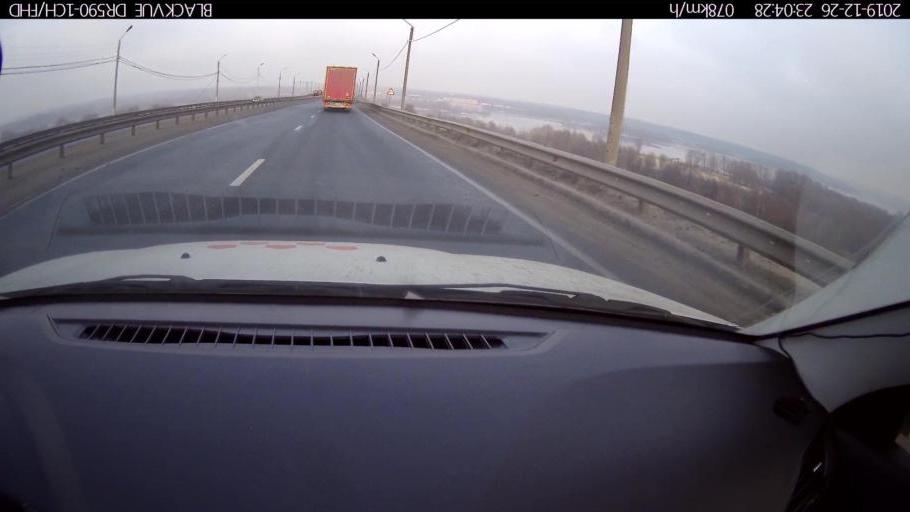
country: RU
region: Nizjnij Novgorod
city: Burevestnik
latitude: 56.1800
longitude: 43.7491
